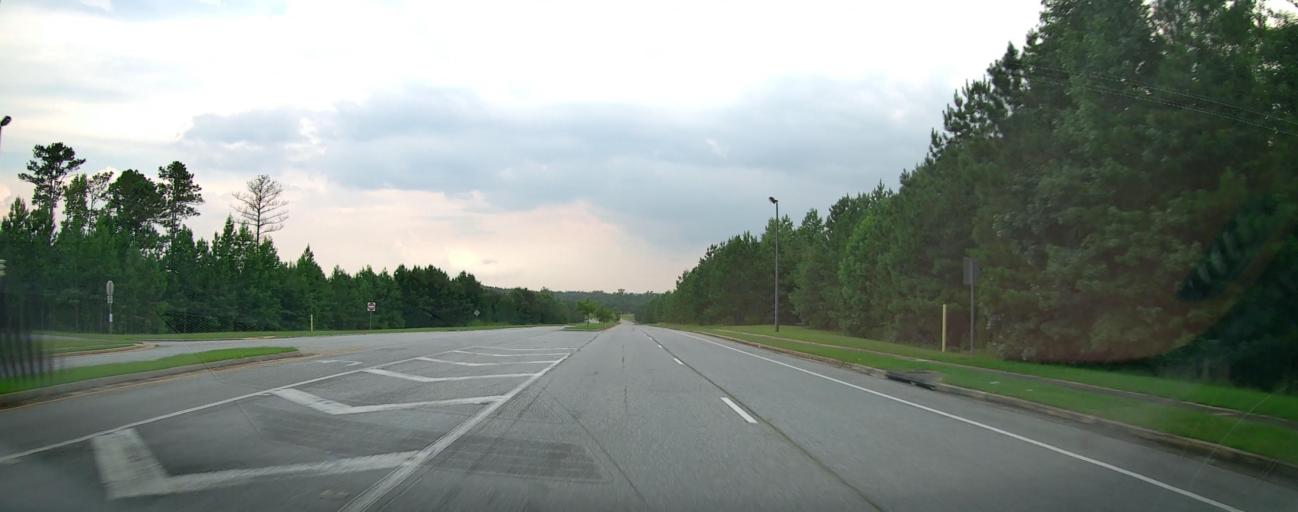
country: US
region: Georgia
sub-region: Muscogee County
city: Columbus
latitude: 32.5240
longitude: -84.8398
